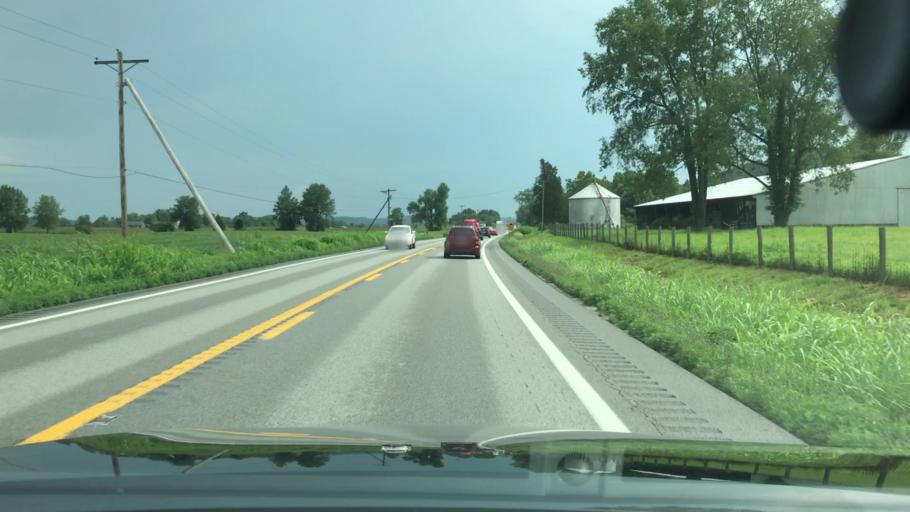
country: US
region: West Virginia
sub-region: Putnam County
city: Buffalo
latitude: 38.6822
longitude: -81.9646
